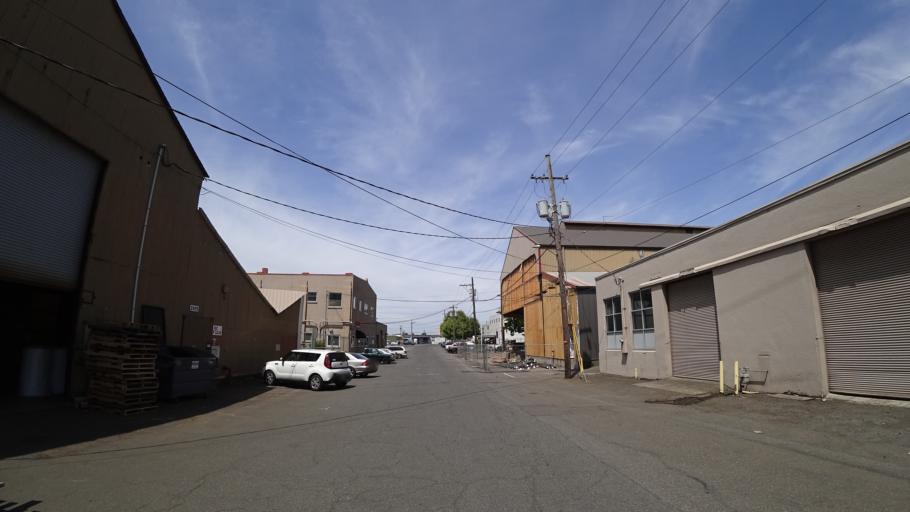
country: US
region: Oregon
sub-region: Multnomah County
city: Portland
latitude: 45.5393
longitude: -122.7092
